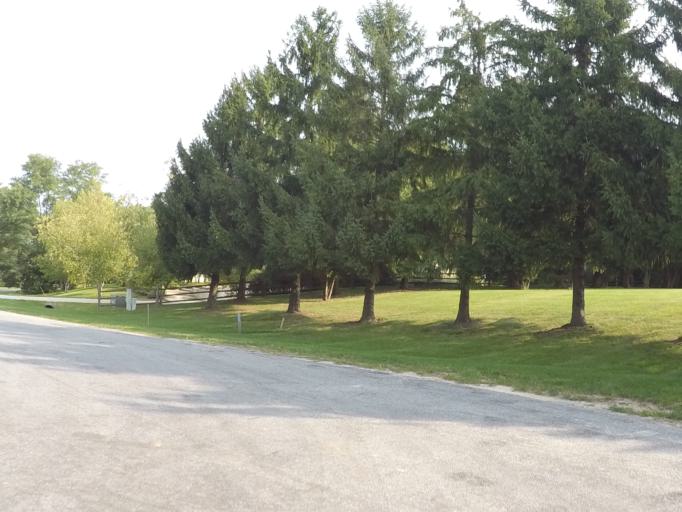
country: US
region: Wisconsin
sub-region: Dane County
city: Verona
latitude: 43.0442
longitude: -89.5296
